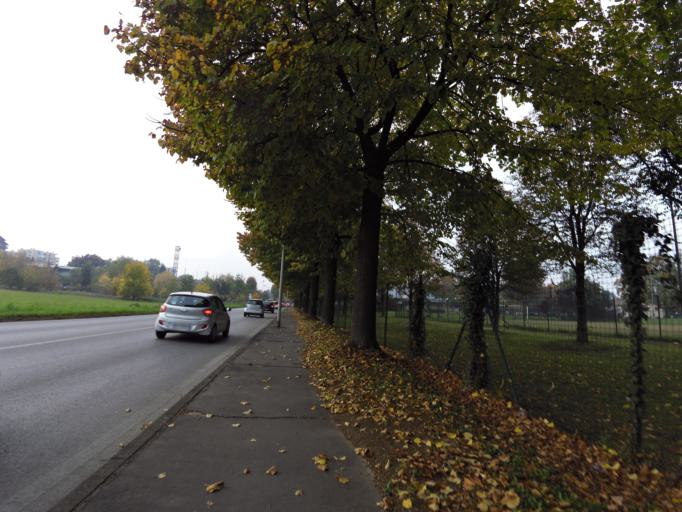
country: IT
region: Lombardy
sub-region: Citta metropolitana di Milano
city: San Donato Milanese
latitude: 45.4138
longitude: 9.2799
